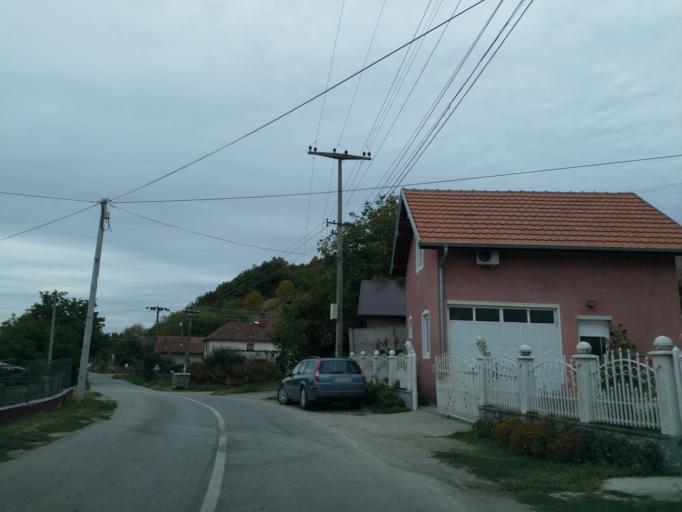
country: RS
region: Central Serbia
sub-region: Pomoravski Okrug
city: Cuprija
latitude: 43.8757
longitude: 21.3195
